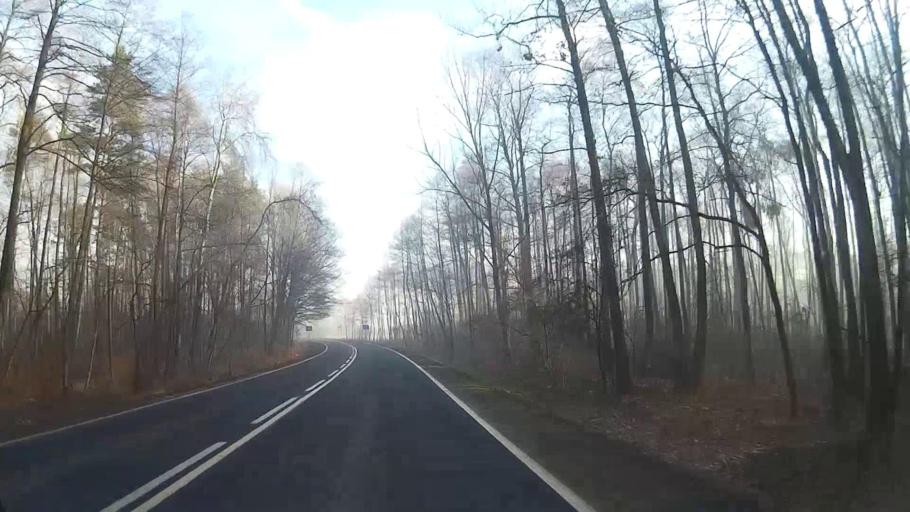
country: PL
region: Lesser Poland Voivodeship
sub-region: Powiat chrzanowski
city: Libiaz
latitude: 50.0832
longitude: 19.2846
